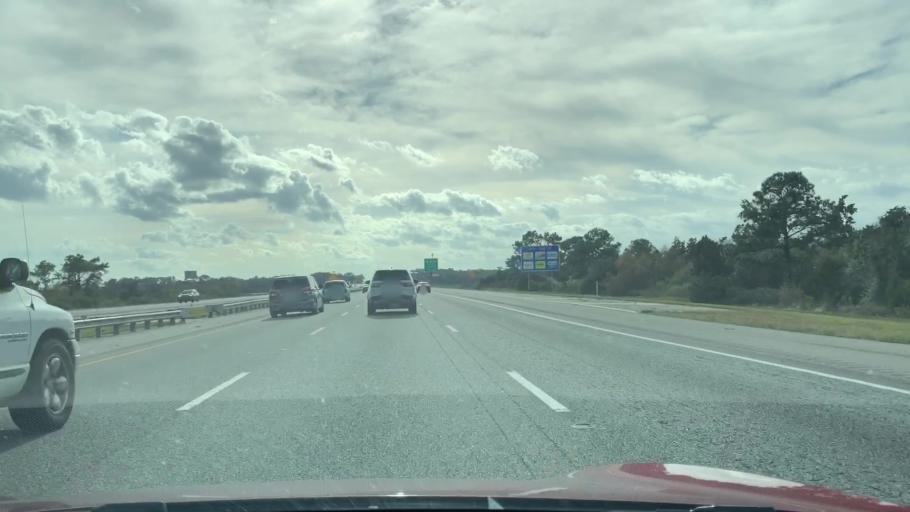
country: US
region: Georgia
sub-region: Glynn County
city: Dock Junction
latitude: 31.1576
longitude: -81.5612
